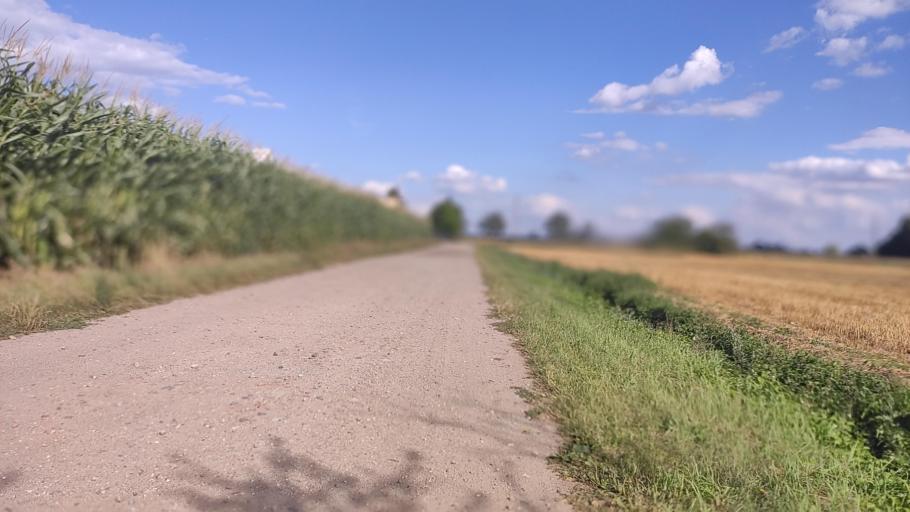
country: PL
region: Greater Poland Voivodeship
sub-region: Powiat poznanski
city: Swarzedz
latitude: 52.4107
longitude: 17.1380
